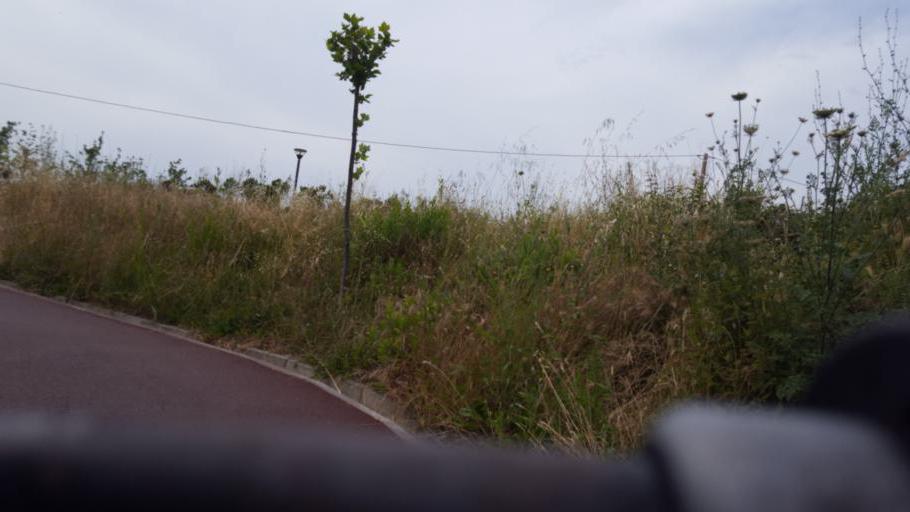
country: AL
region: Tirane
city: Tirana
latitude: 41.3068
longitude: 19.8199
